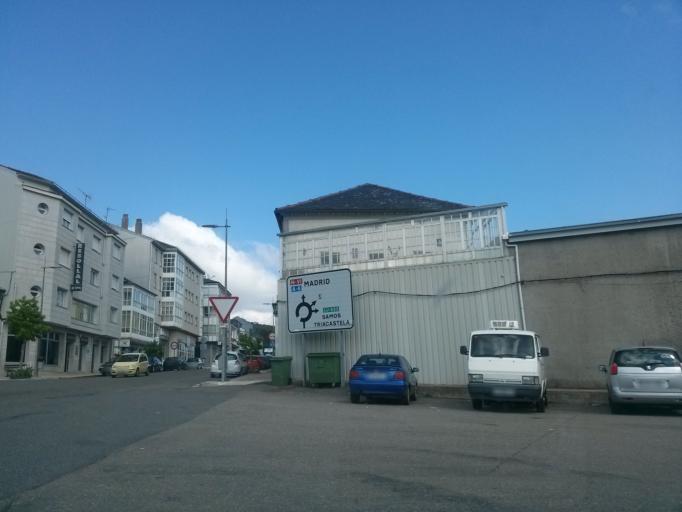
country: ES
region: Castille and Leon
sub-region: Provincia de Leon
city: Balboa
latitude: 42.7266
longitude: -7.0222
